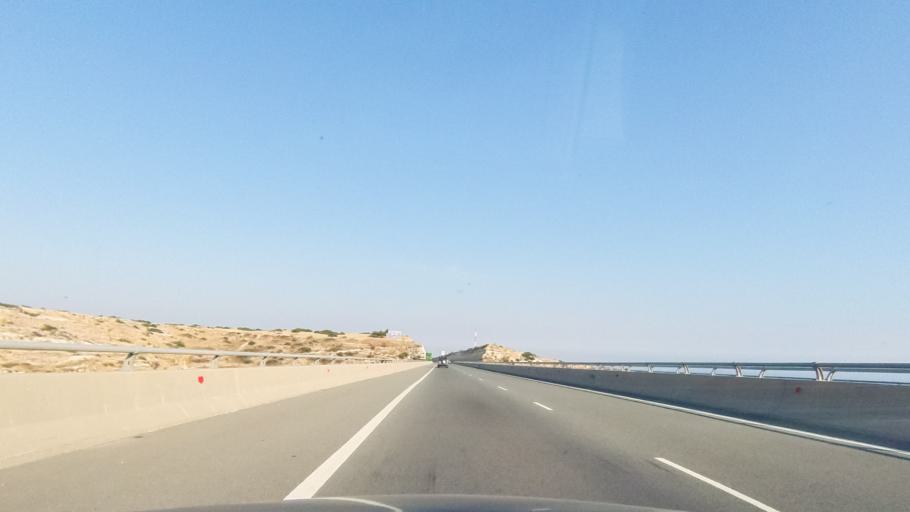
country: CY
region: Limassol
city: Sotira
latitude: 34.6890
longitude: 32.8724
